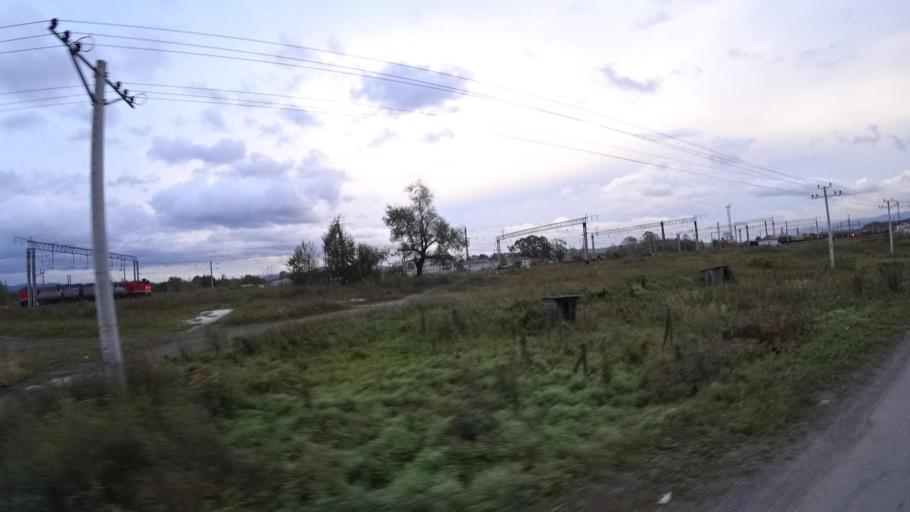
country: RU
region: Jewish Autonomous Oblast
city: Izvestkovyy
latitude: 48.9862
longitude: 131.5486
